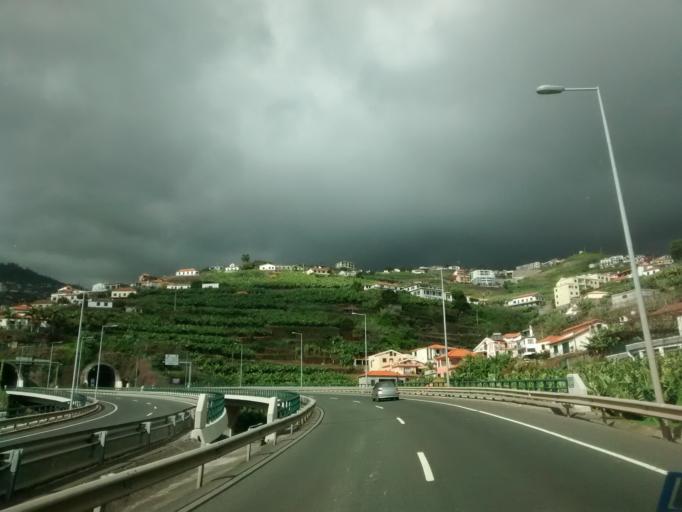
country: PT
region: Madeira
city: Camara de Lobos
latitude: 32.6597
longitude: -16.9764
